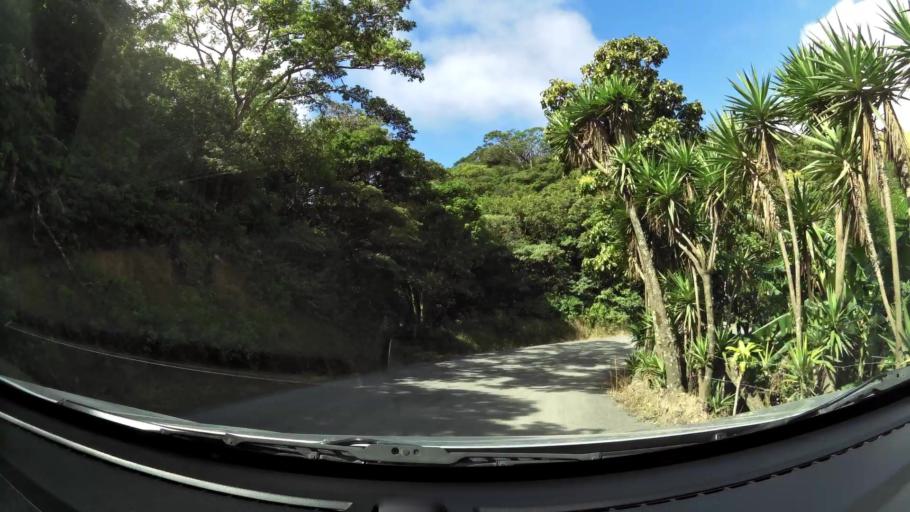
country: CR
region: Guanacaste
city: Juntas
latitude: 10.3427
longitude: -84.9022
